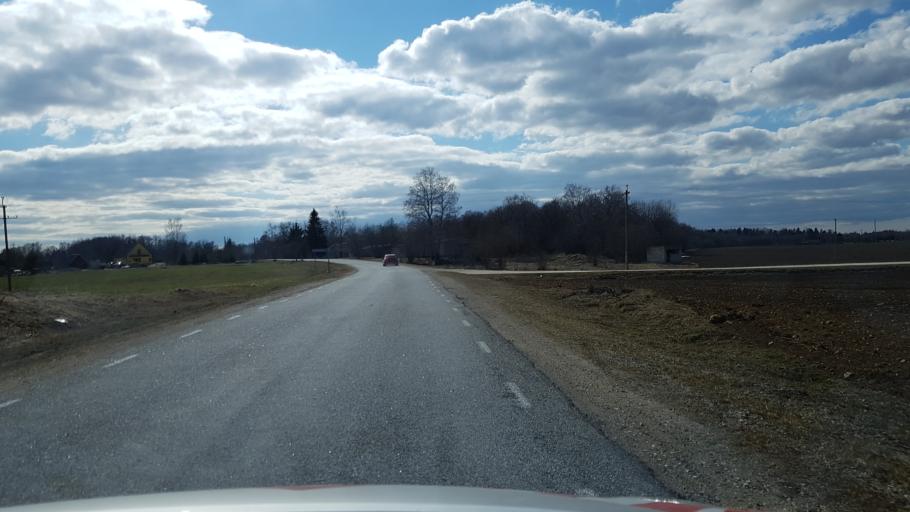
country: EE
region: Laeaene-Virumaa
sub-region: Rakvere linn
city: Rakvere
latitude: 59.3270
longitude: 26.2756
